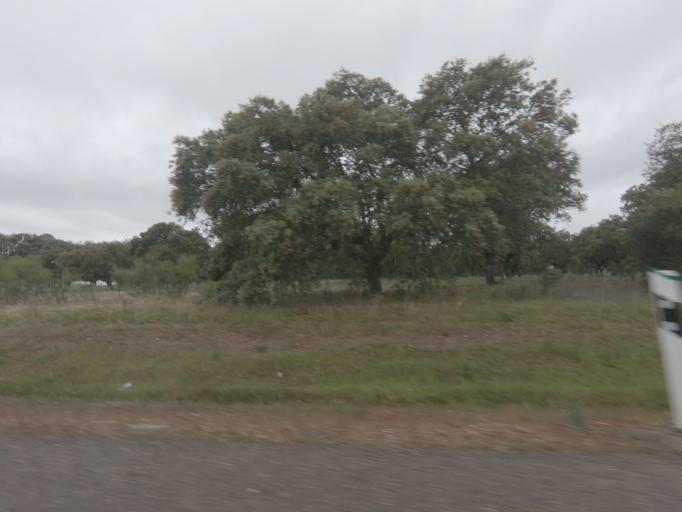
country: ES
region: Extremadura
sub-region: Provincia de Badajoz
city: Villar del Rey
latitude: 39.0457
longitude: -6.8062
